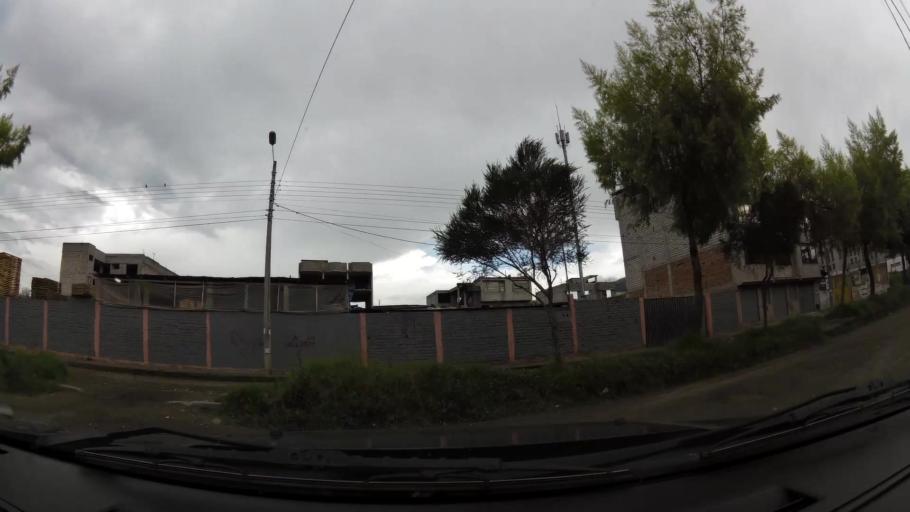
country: EC
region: Pichincha
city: Quito
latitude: -0.3100
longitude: -78.5539
